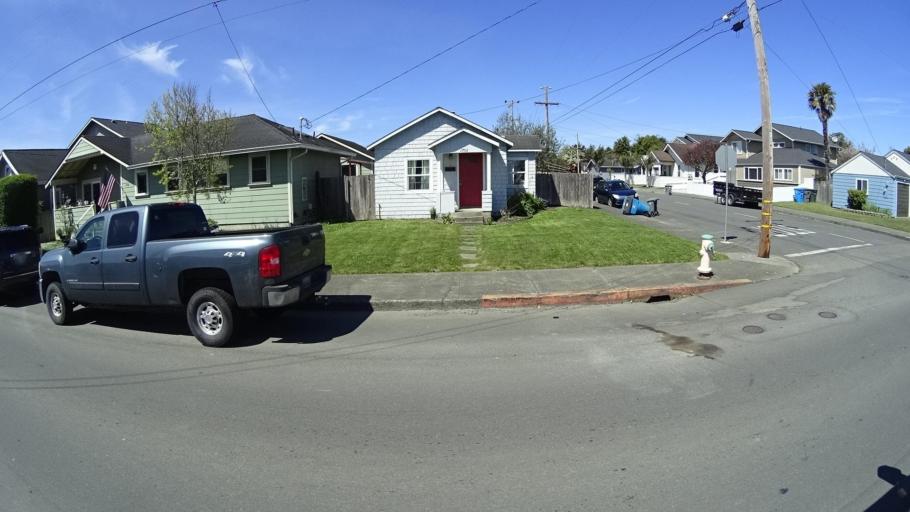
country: US
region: California
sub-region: Humboldt County
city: Eureka
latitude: 40.7937
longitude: -124.1481
